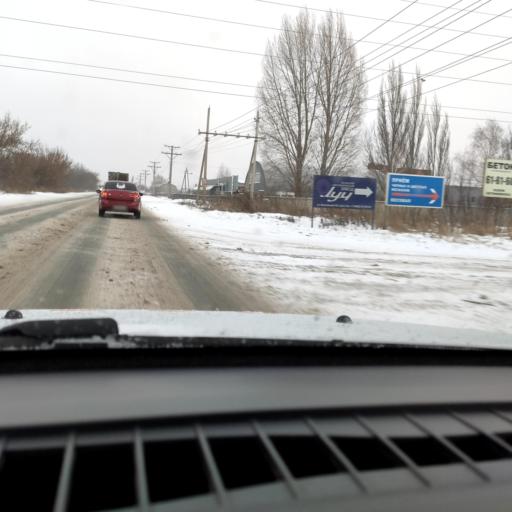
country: RU
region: Samara
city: Tol'yatti
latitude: 53.5779
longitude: 49.2996
